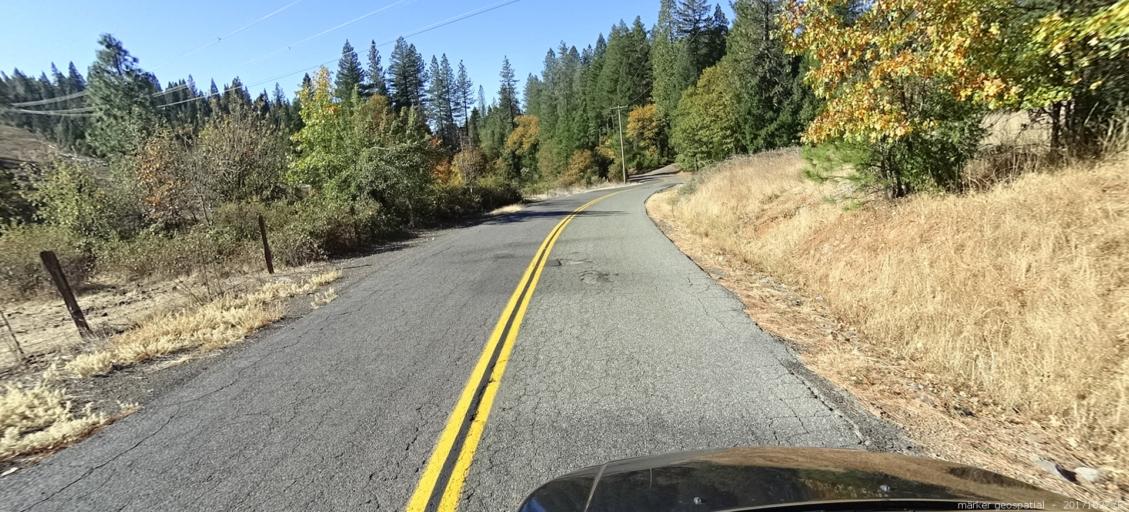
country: US
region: California
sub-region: Shasta County
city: Bella Vista
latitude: 40.8193
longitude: -121.9712
